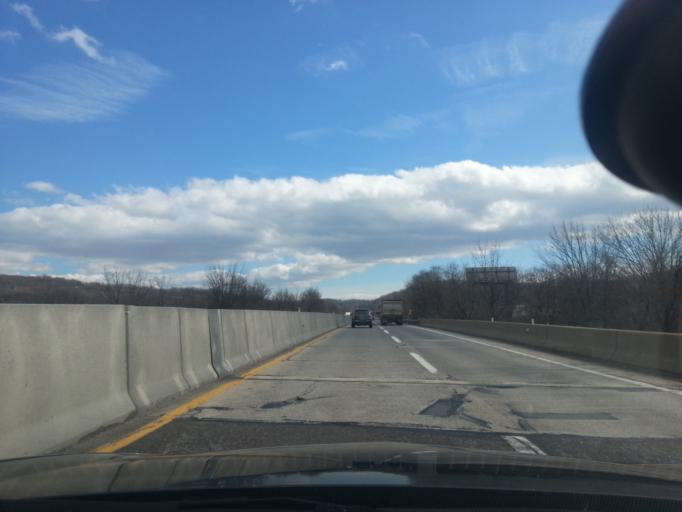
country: US
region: Pennsylvania
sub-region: Lehigh County
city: Emmaus
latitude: 40.5257
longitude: -75.5155
